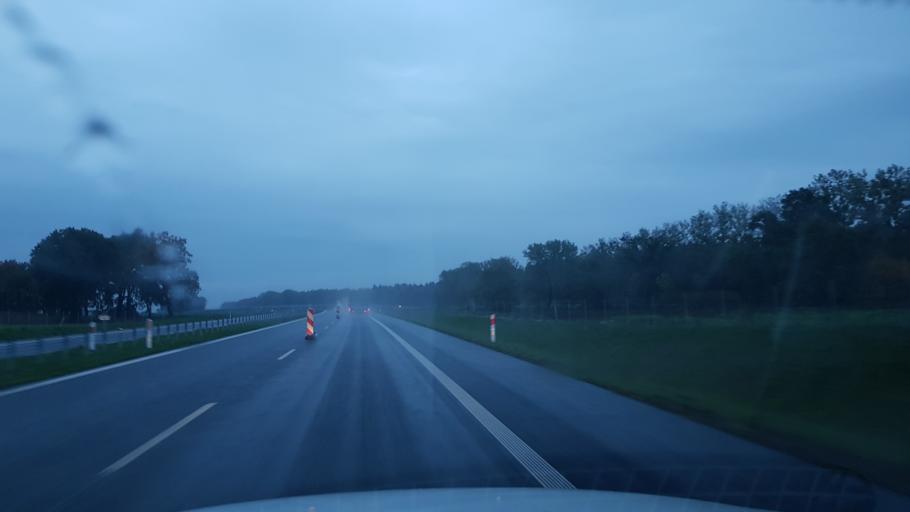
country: PL
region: West Pomeranian Voivodeship
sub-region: Powiat gryficki
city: Ploty
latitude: 53.8304
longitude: 15.2885
